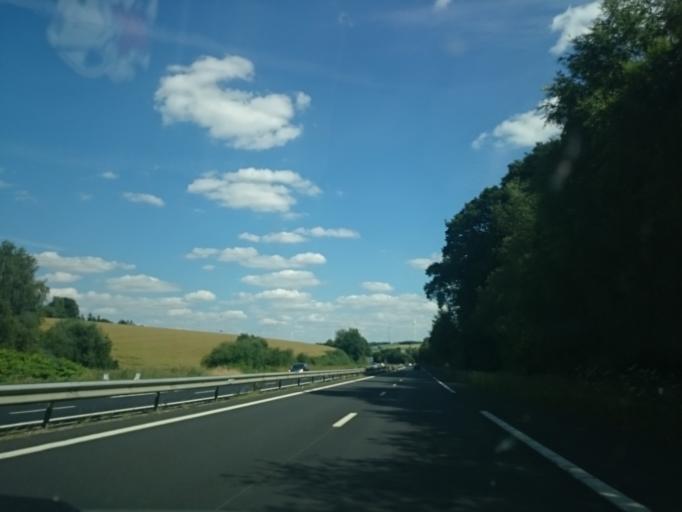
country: FR
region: Brittany
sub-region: Departement des Cotes-d'Armor
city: Plemet
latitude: 48.1714
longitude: -2.6514
